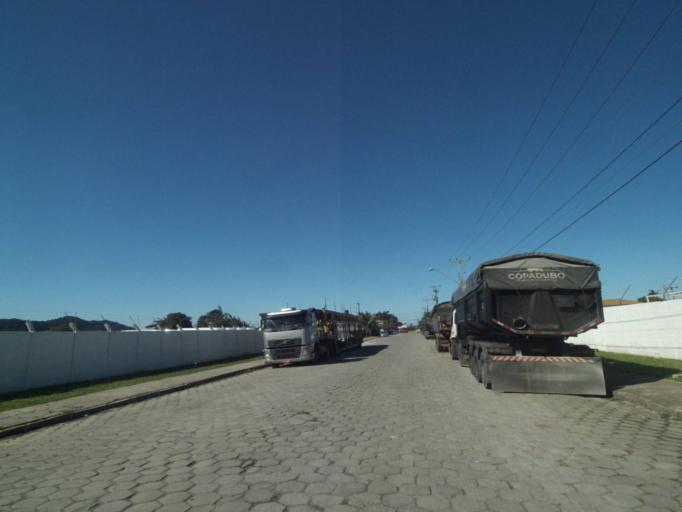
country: BR
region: Parana
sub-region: Paranagua
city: Paranagua
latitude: -25.5099
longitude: -48.5057
